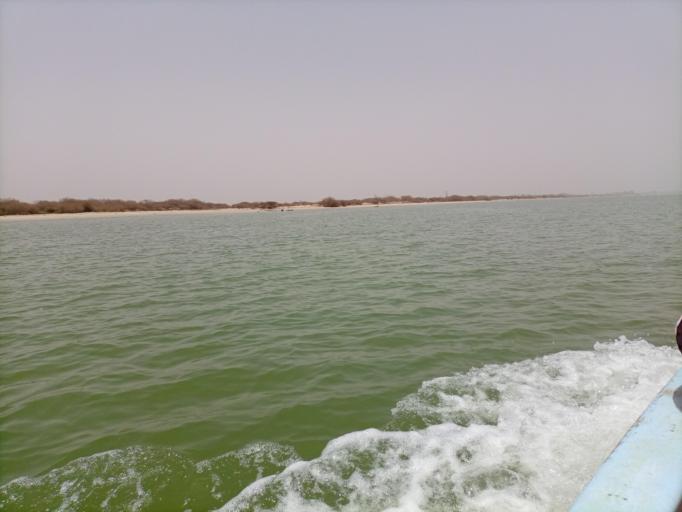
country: SN
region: Saint-Louis
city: Saint-Louis
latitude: 15.8627
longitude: -16.5149
